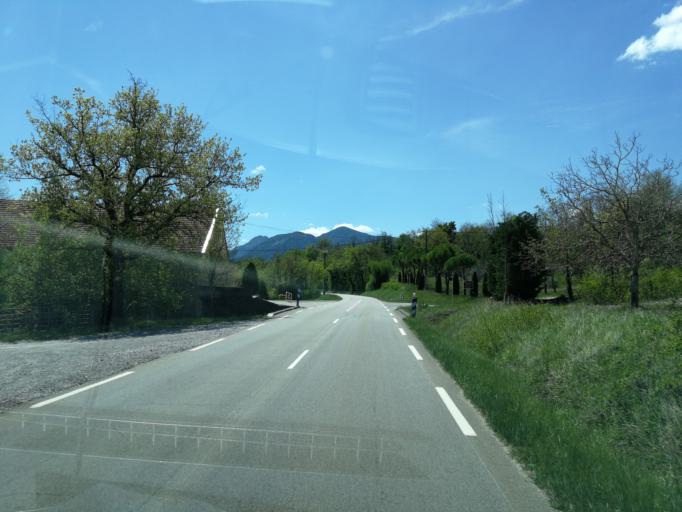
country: FR
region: Rhone-Alpes
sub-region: Departement de la Drome
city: Die
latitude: 44.7294
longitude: 5.2665
